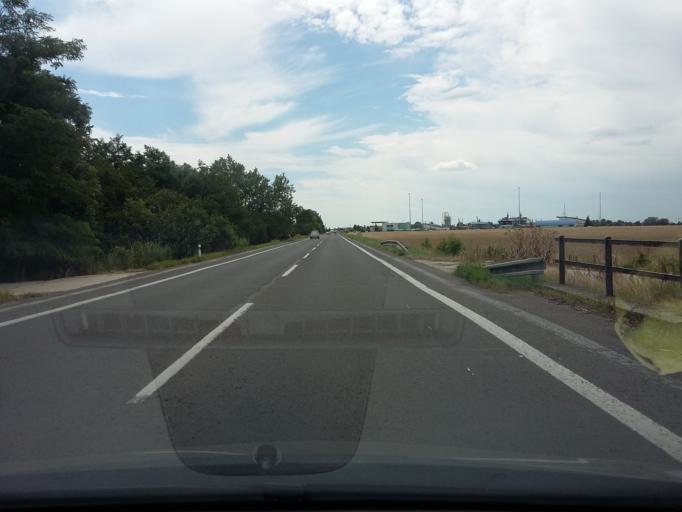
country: SK
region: Bratislavsky
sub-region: Okres Malacky
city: Malacky
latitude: 48.4564
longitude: 17.0105
